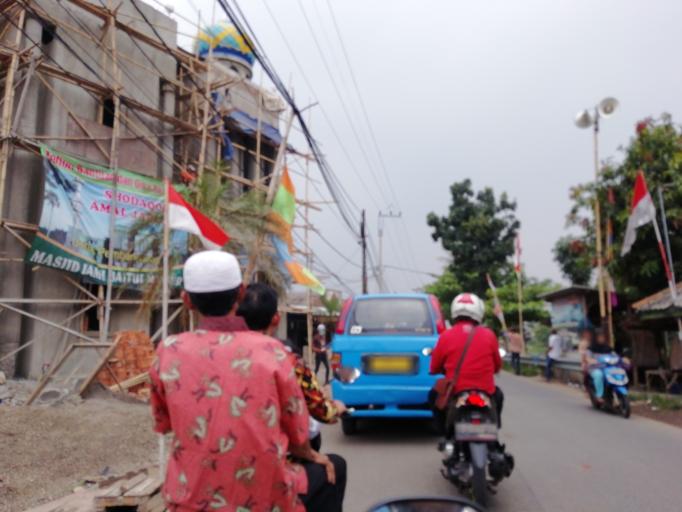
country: ID
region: West Java
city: Cibinong
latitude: -6.4694
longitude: 106.8040
